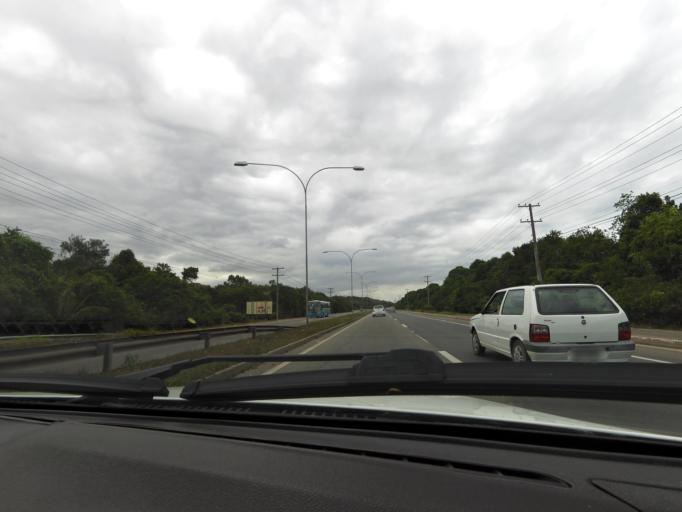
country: BR
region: Espirito Santo
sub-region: Vila Velha
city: Vila Velha
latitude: -20.4085
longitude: -40.3268
